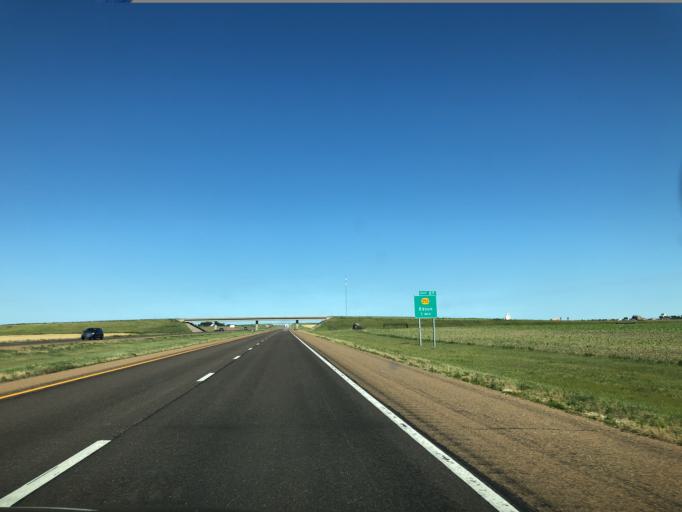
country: US
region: Kansas
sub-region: Sherman County
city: Goodland
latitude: 39.3300
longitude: -101.5171
